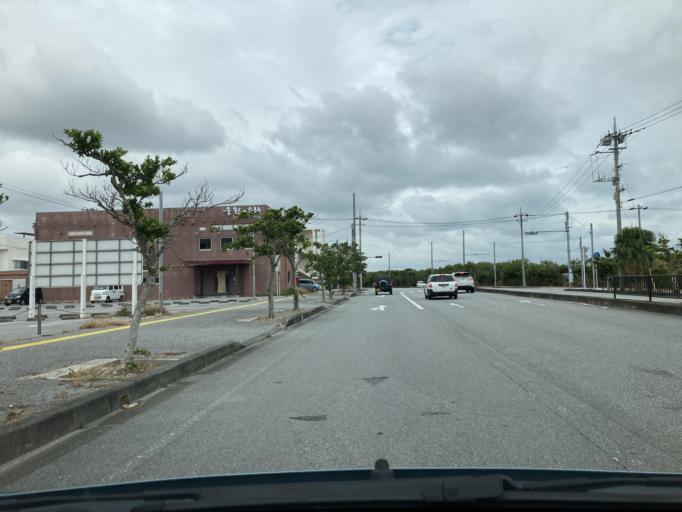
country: JP
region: Okinawa
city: Ginowan
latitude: 26.2086
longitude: 127.7637
